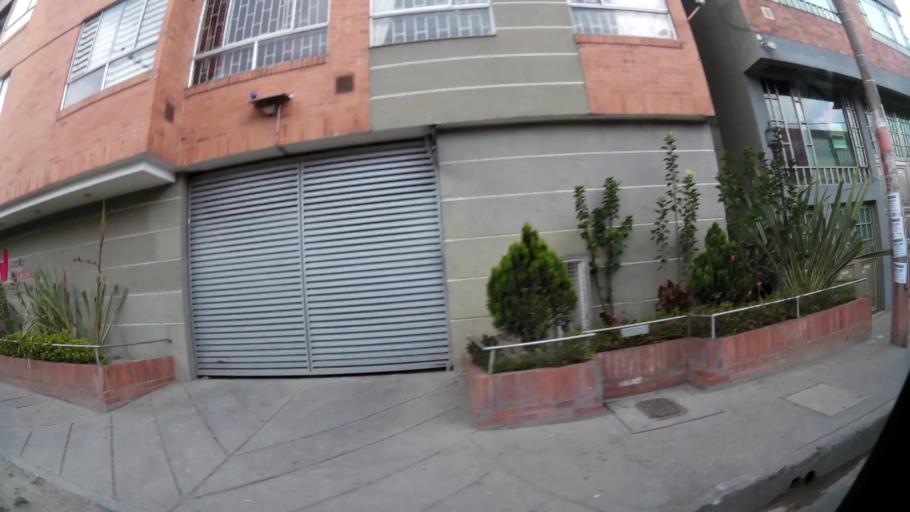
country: CO
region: Cundinamarca
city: La Calera
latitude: 4.7385
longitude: -74.0263
